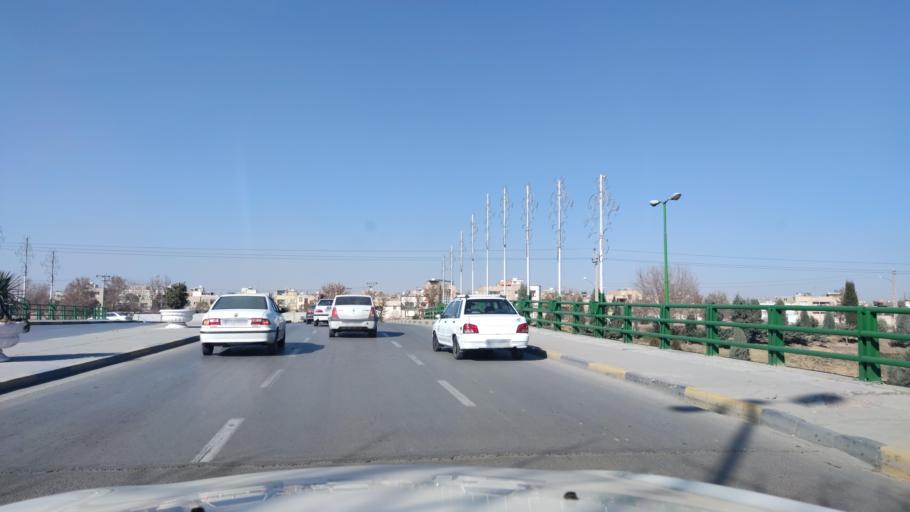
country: IR
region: Isfahan
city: Isfahan
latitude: 32.6827
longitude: 51.6466
